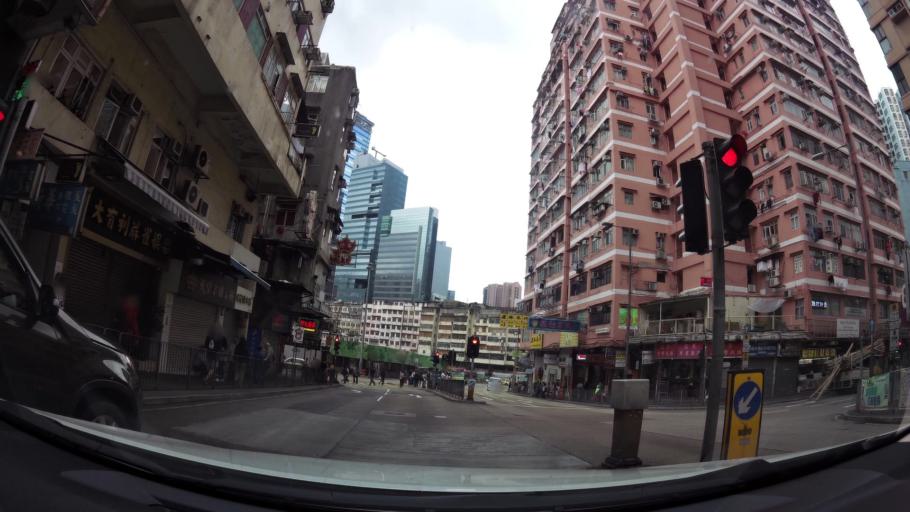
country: HK
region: Kowloon City
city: Kowloon
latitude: 22.3152
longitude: 114.2237
